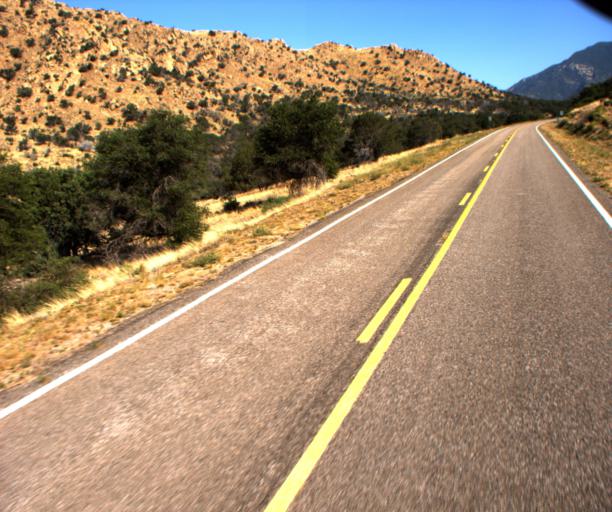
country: US
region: Arizona
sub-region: Graham County
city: Swift Trail Junction
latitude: 32.5834
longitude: -109.8529
